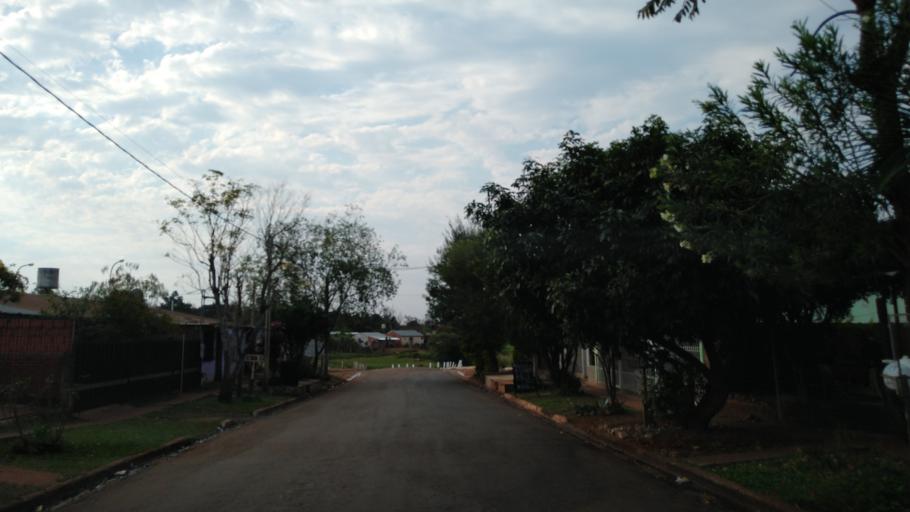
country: AR
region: Misiones
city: Garupa
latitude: -27.4329
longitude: -55.8754
